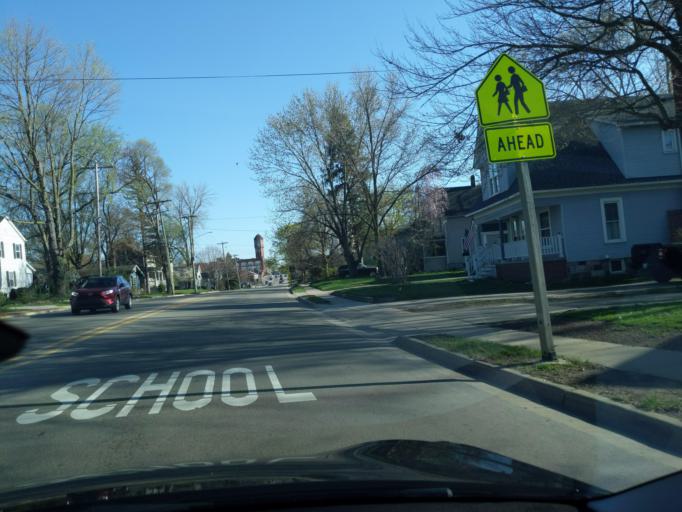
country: US
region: Michigan
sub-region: Washtenaw County
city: Chelsea
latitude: 42.3234
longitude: -84.0207
